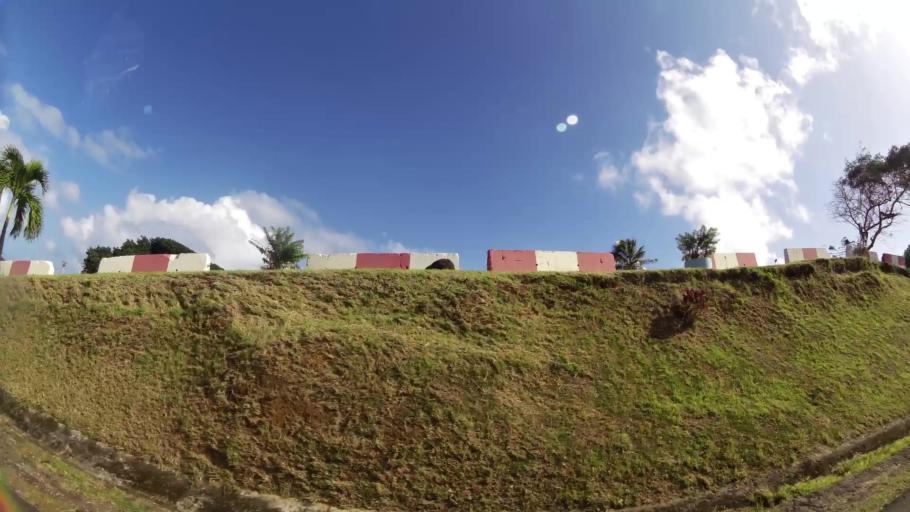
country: MQ
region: Martinique
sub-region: Martinique
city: Sainte-Marie
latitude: 14.7832
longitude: -60.9941
